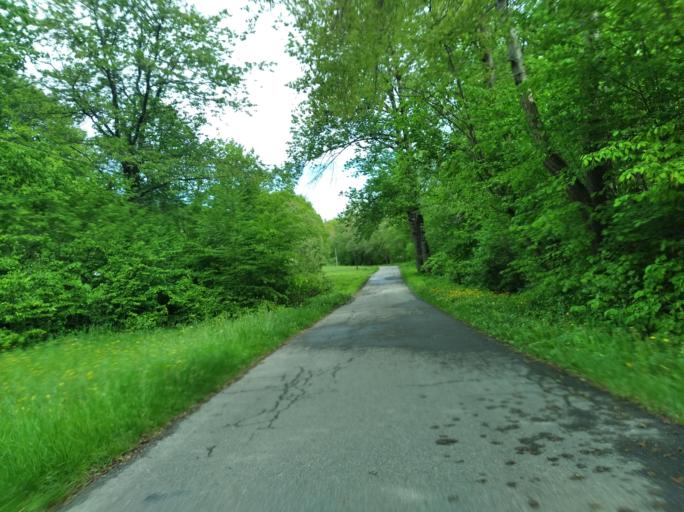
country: PL
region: Subcarpathian Voivodeship
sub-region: Powiat strzyzowski
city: Strzyzow
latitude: 49.9223
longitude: 21.7540
